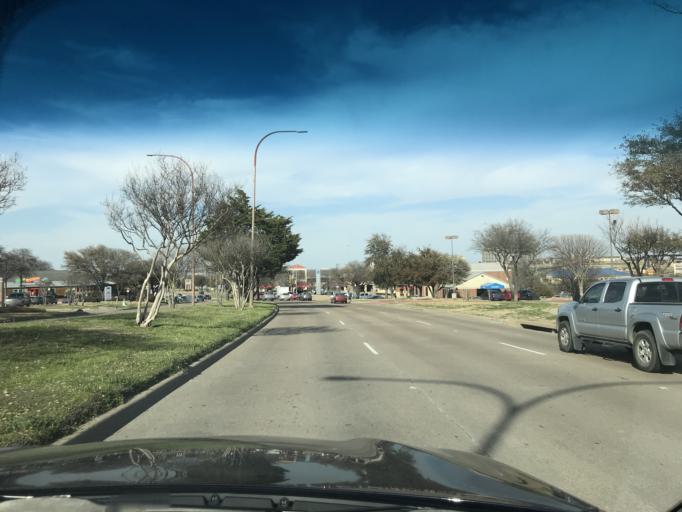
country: US
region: Texas
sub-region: Tarrant County
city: Benbrook
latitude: 32.6790
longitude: -97.4151
